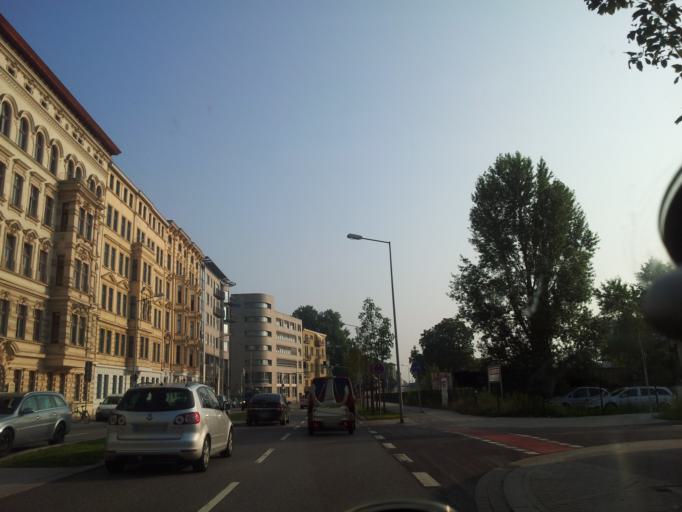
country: DE
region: Saxony-Anhalt
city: Magdeburg
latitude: 52.1201
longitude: 11.6325
